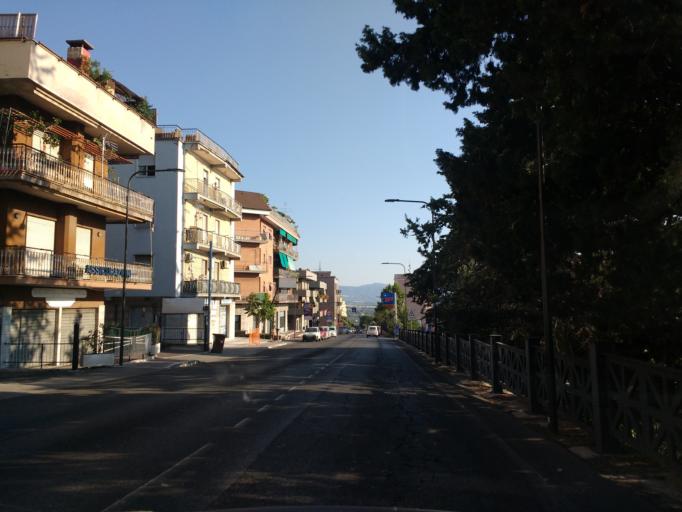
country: IT
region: Latium
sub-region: Citta metropolitana di Roma Capitale
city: Tivoli
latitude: 41.9551
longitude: 12.7919
